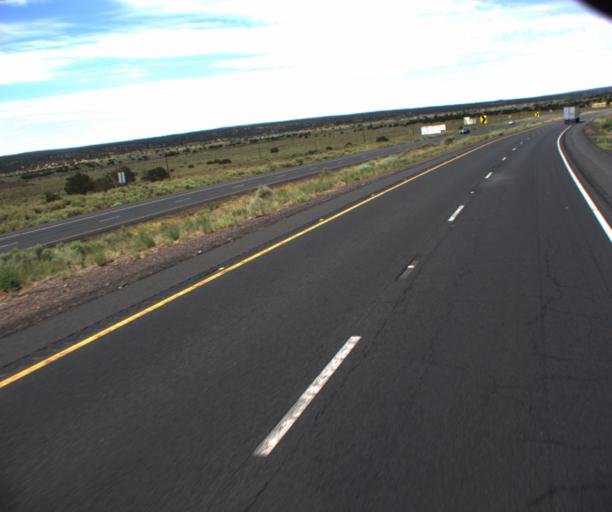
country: US
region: Arizona
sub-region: Apache County
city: Houck
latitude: 35.2810
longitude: -109.1762
